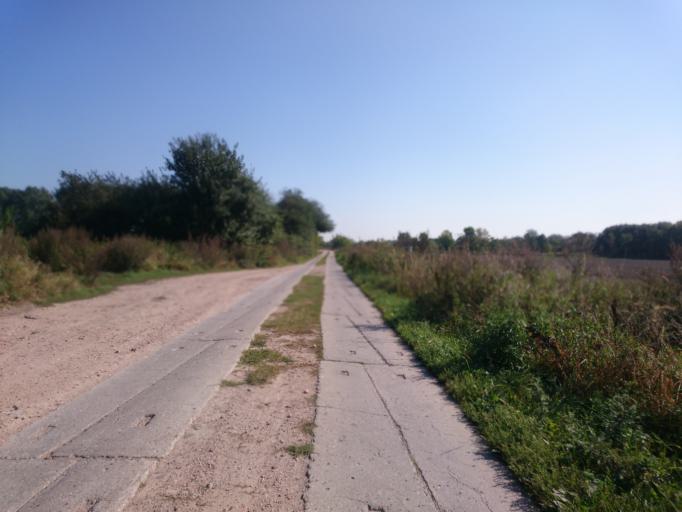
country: DE
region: Mecklenburg-Vorpommern
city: Barth
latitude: 54.3576
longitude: 12.7022
